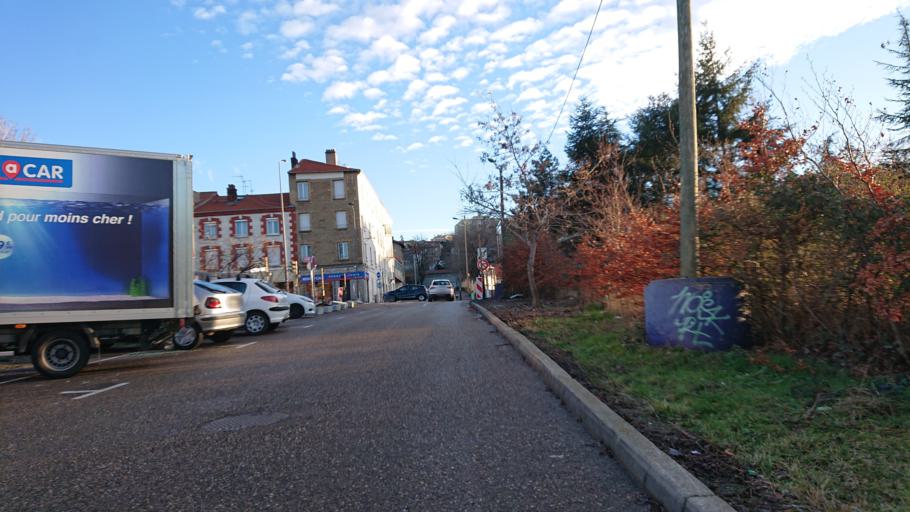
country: FR
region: Rhone-Alpes
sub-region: Departement de la Loire
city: Saint-Etienne
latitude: 45.4433
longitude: 4.4112
